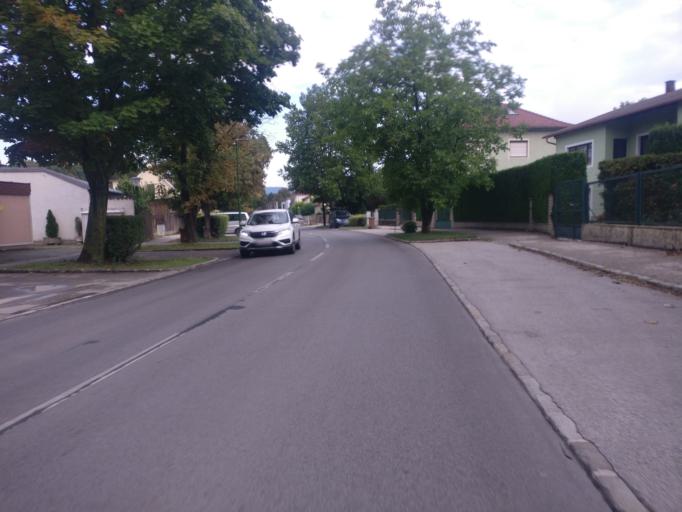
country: AT
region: Lower Austria
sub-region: Politischer Bezirk Modling
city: Guntramsdorf
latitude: 48.0456
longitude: 16.3206
